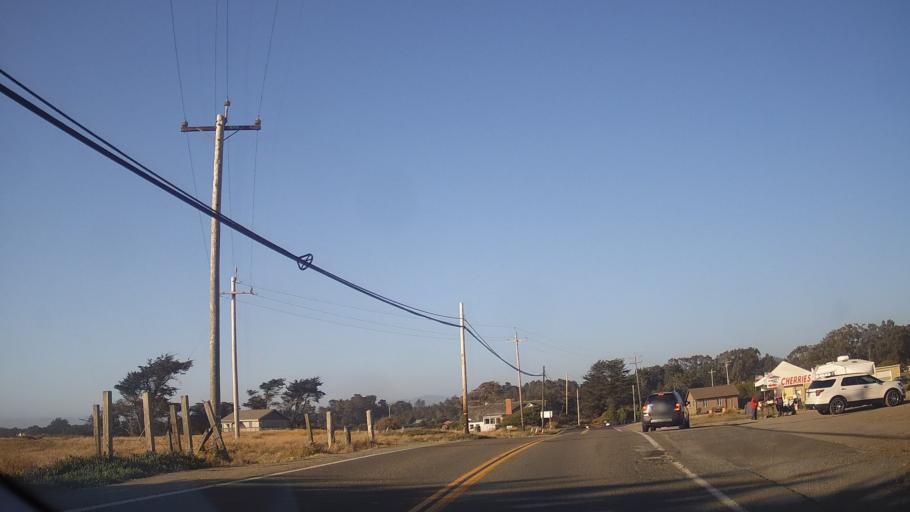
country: US
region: California
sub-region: Mendocino County
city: Fort Bragg
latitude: 39.4685
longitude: -123.8030
